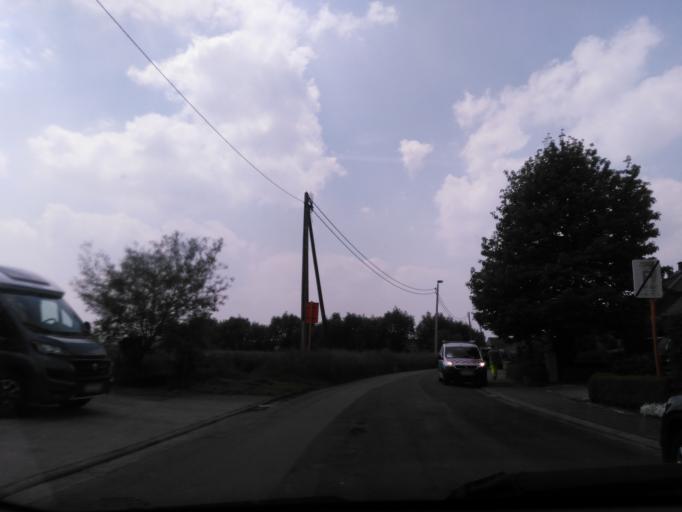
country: BE
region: Flanders
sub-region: Provincie Oost-Vlaanderen
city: Beveren
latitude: 51.2127
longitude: 4.2827
